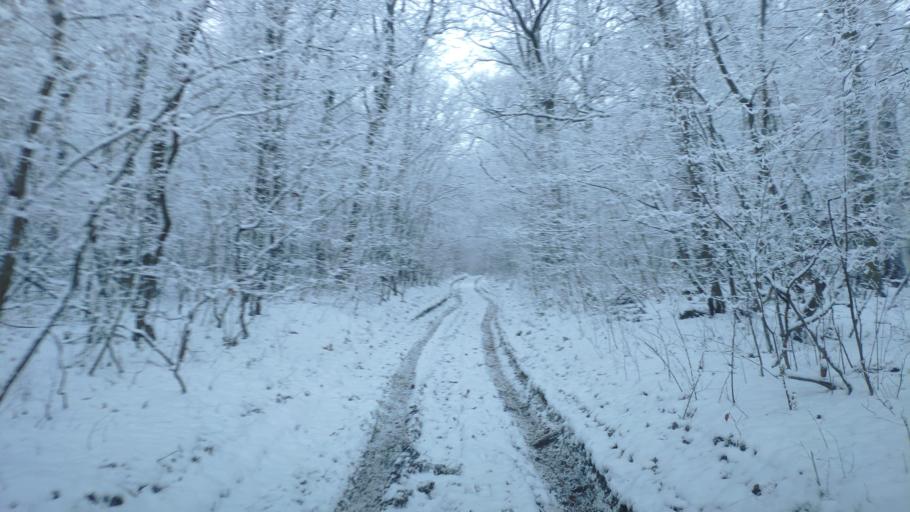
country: SK
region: Kosicky
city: Kosice
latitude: 48.6438
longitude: 21.1903
